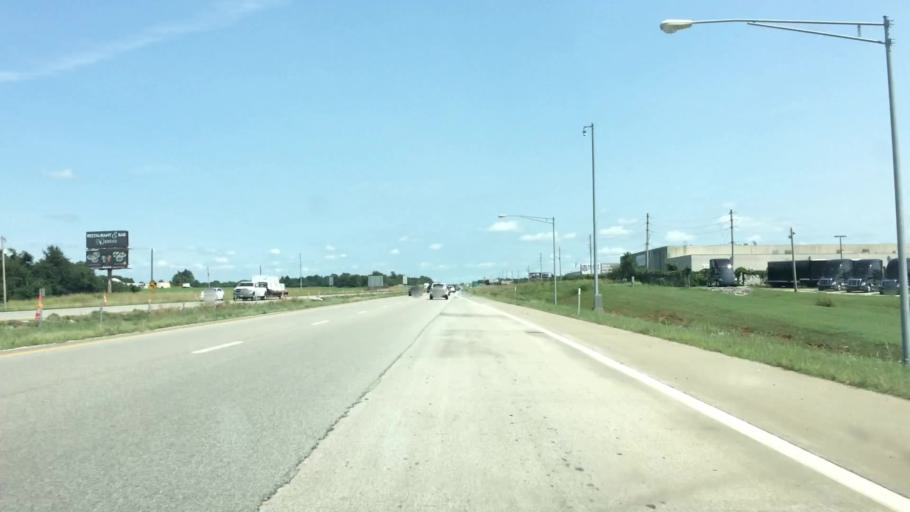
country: US
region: Missouri
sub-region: Greene County
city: Springfield
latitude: 37.2501
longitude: -93.2154
